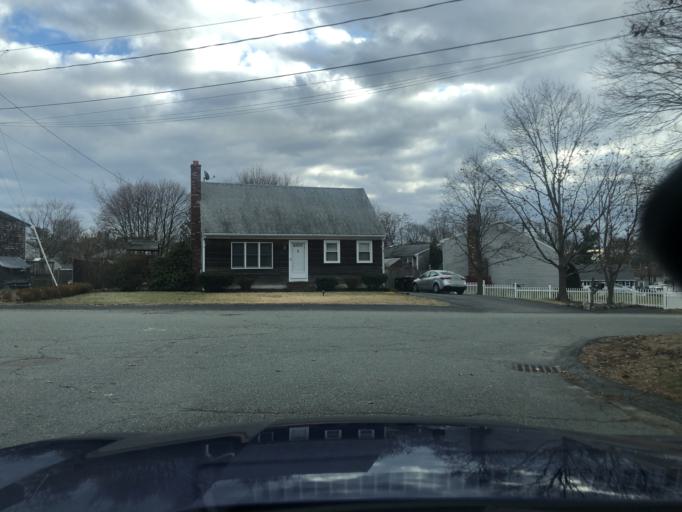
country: US
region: Massachusetts
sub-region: Plymouth County
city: Brockton
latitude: 42.1048
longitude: -71.0149
